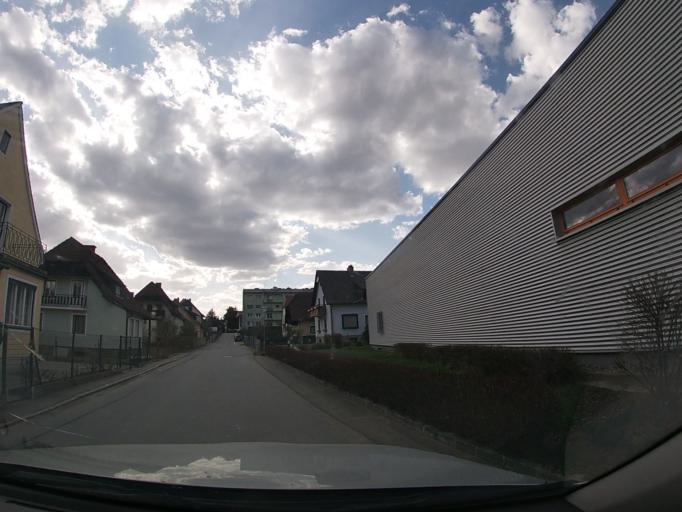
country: AT
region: Styria
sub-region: Politischer Bezirk Murau
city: Murau
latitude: 47.1112
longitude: 14.1810
